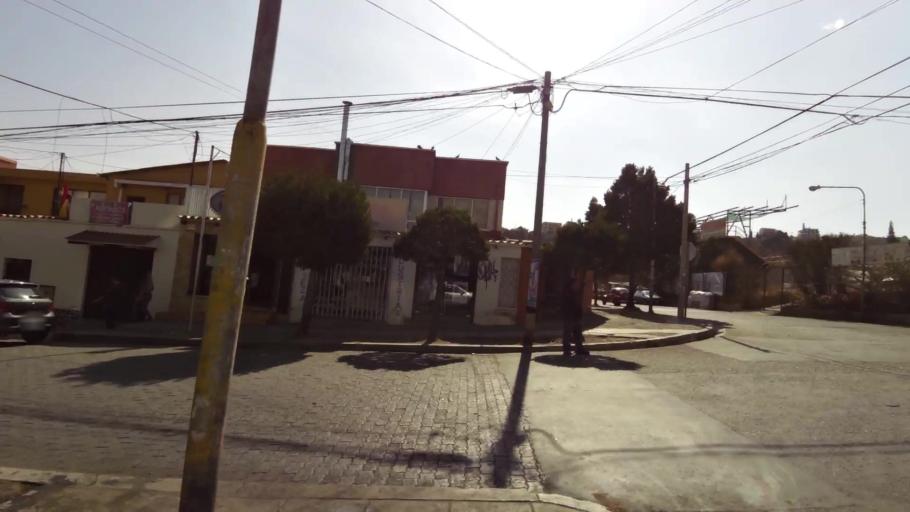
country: BO
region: La Paz
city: La Paz
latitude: -16.5320
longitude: -68.0737
